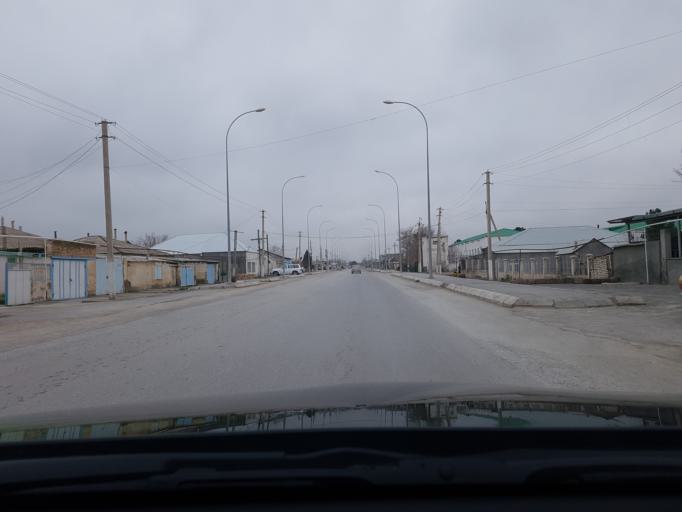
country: TM
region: Ahal
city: Abadan
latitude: 38.1554
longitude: 57.9574
